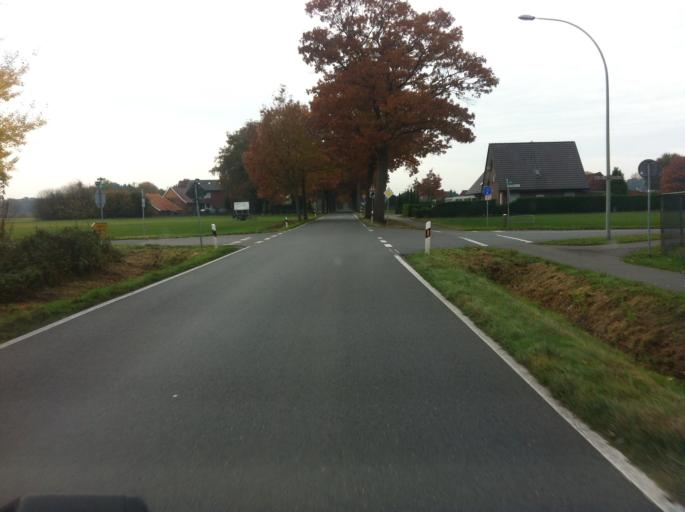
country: DE
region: North Rhine-Westphalia
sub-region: Regierungsbezirk Munster
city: Vreden
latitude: 52.0170
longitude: 6.7989
